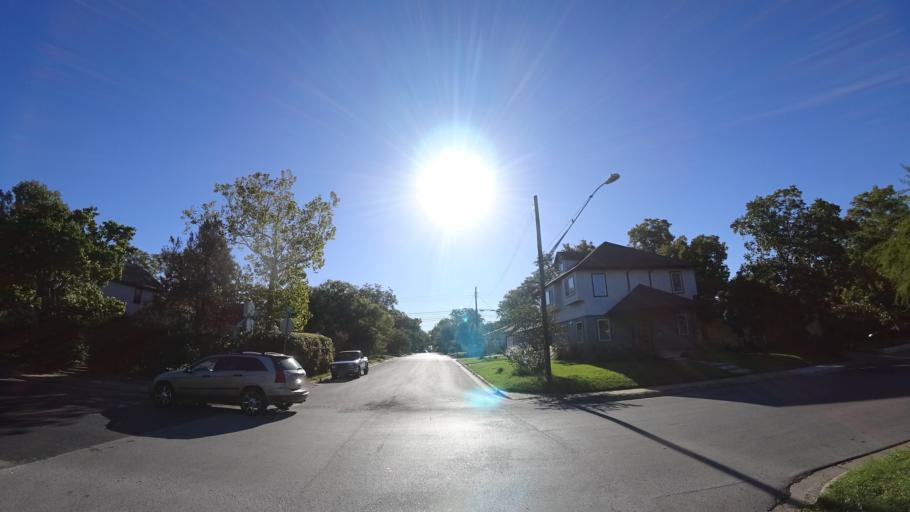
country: US
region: Texas
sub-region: Travis County
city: Austin
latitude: 30.3188
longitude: -97.7206
